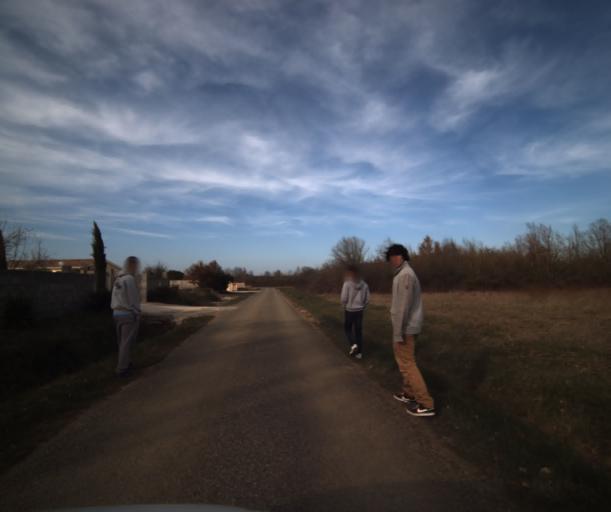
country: FR
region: Midi-Pyrenees
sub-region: Departement du Tarn-et-Garonne
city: Labastide-Saint-Pierre
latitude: 43.9094
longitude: 1.3746
